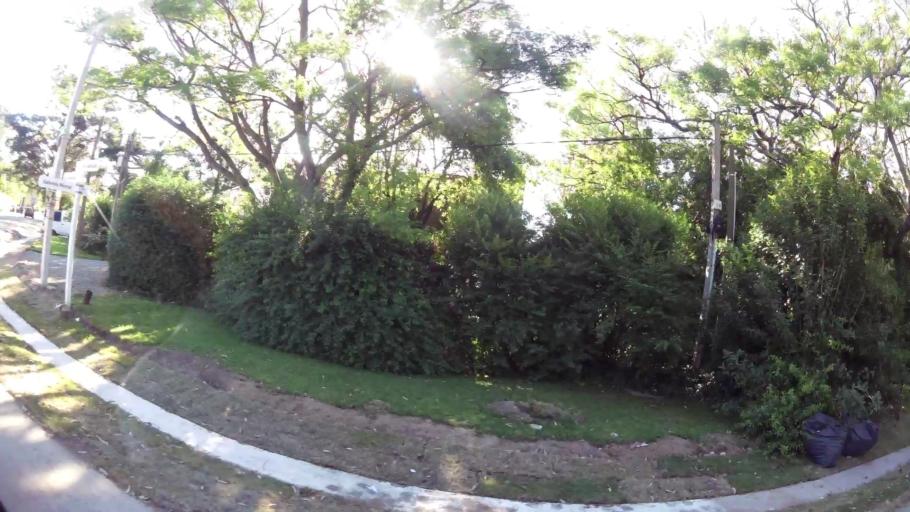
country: UY
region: Canelones
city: Barra de Carrasco
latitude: -34.8651
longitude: -56.0341
